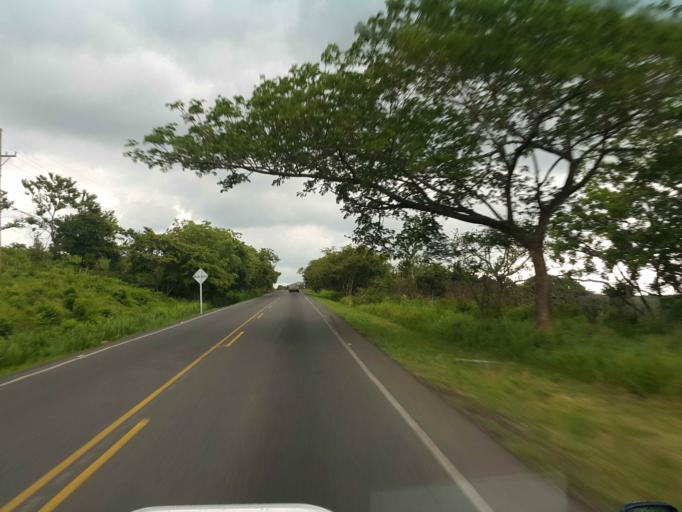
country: CR
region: Puntarenas
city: Miramar
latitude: 10.0999
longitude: -84.8048
